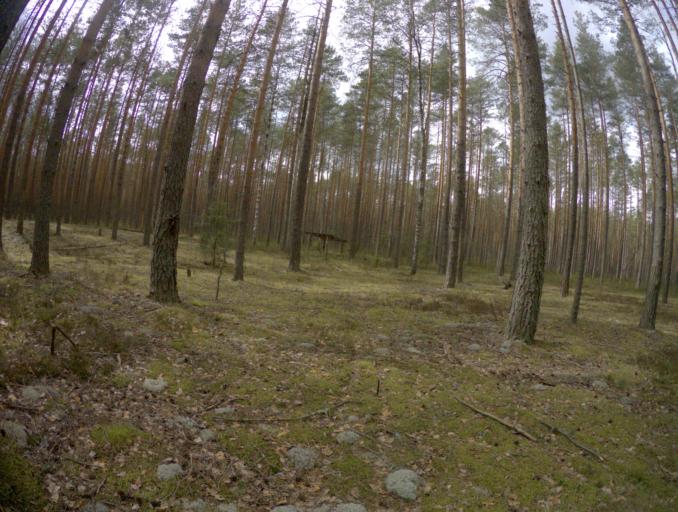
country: RU
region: Vladimir
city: Raduzhnyy
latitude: 55.9485
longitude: 40.2749
